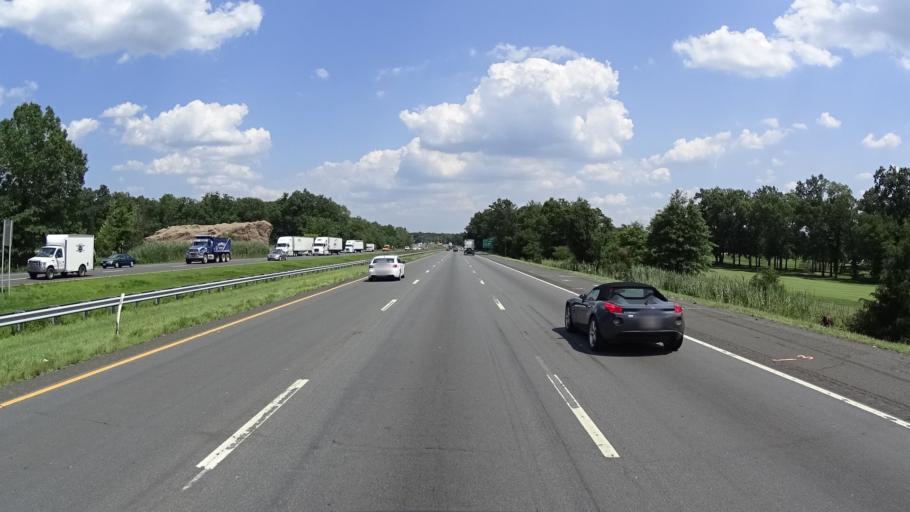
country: US
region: New Jersey
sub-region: Hunterdon County
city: Whitehouse Station
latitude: 40.6466
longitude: -74.7300
